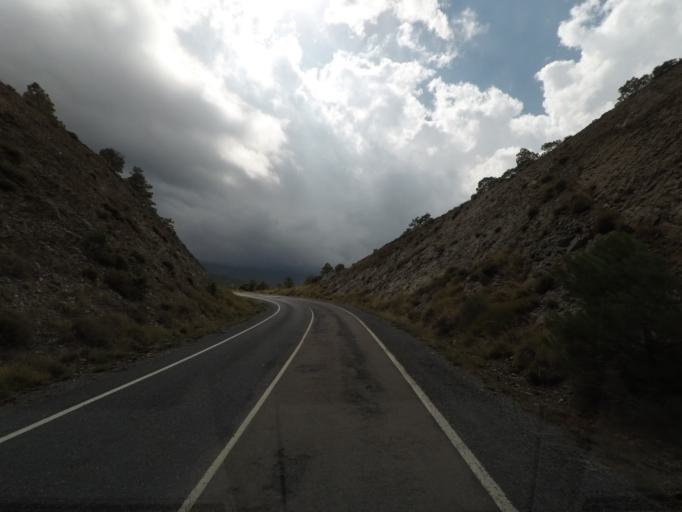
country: ES
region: Andalusia
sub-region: Provincia de Granada
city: Aldeire
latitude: 37.1514
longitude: -3.0504
